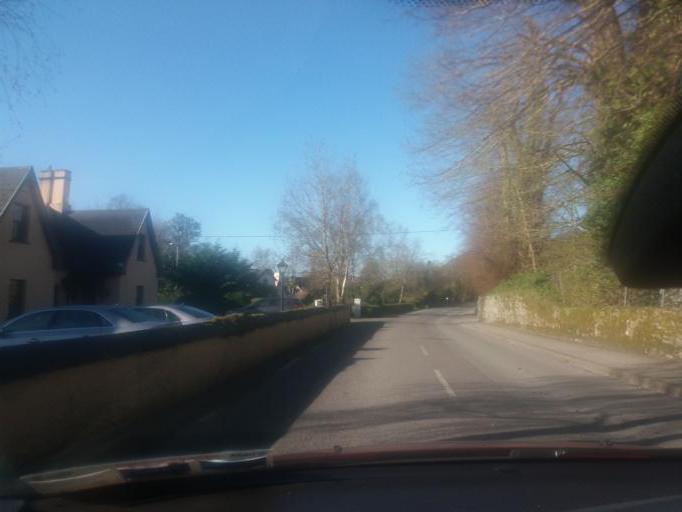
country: IE
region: Munster
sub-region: Ciarrai
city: Cill Airne
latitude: 52.0474
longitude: -9.5208
